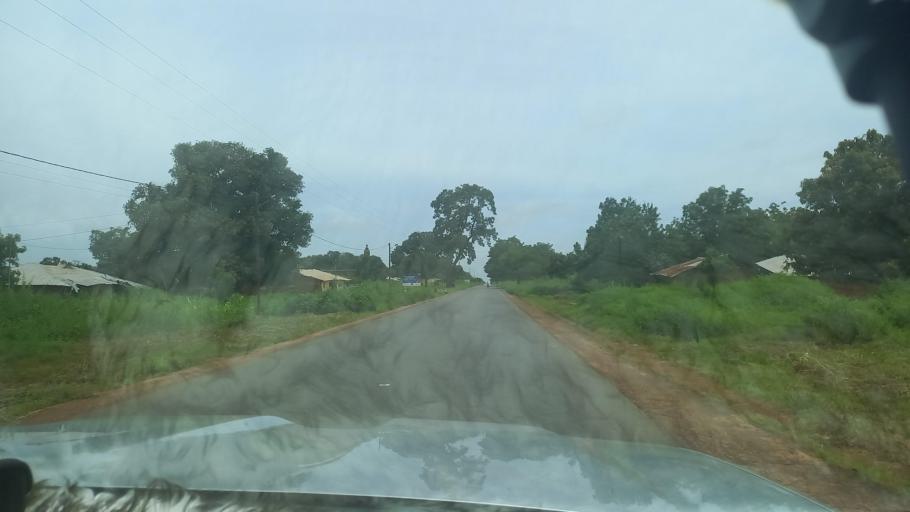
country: SN
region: Kolda
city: Marsassoum
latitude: 12.9615
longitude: -15.9879
